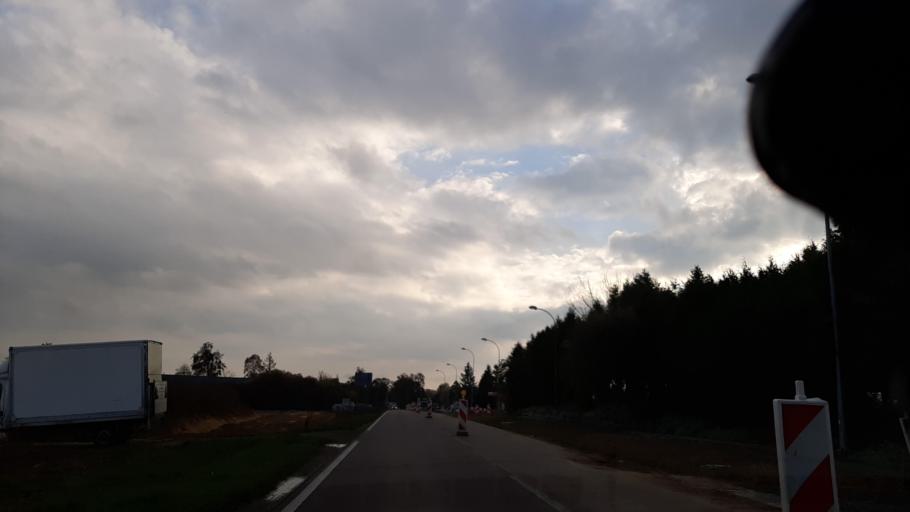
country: PL
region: Lublin Voivodeship
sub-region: Powiat pulawski
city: Naleczow
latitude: 51.3106
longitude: 22.2204
